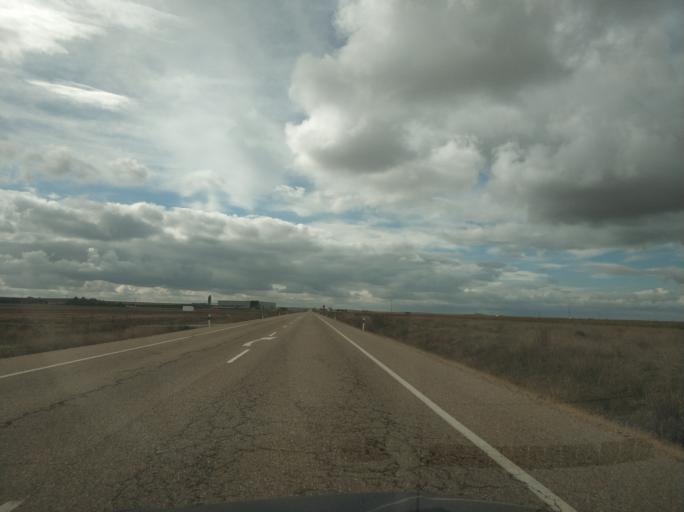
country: ES
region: Castille and Leon
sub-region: Provincia de Valladolid
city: Pollos
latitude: 41.4310
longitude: -5.1074
